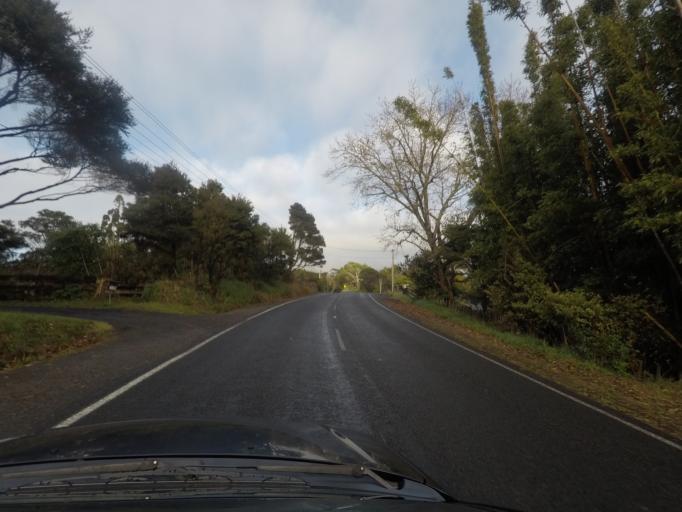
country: NZ
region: Auckland
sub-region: Auckland
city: Waitakere
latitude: -36.9114
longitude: 174.6080
